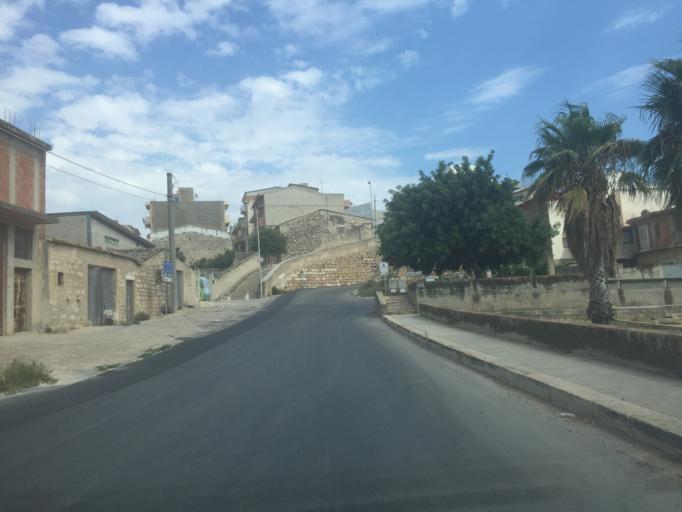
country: IT
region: Sicily
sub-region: Ragusa
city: Santa Croce Camerina
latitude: 36.8301
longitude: 14.5213
